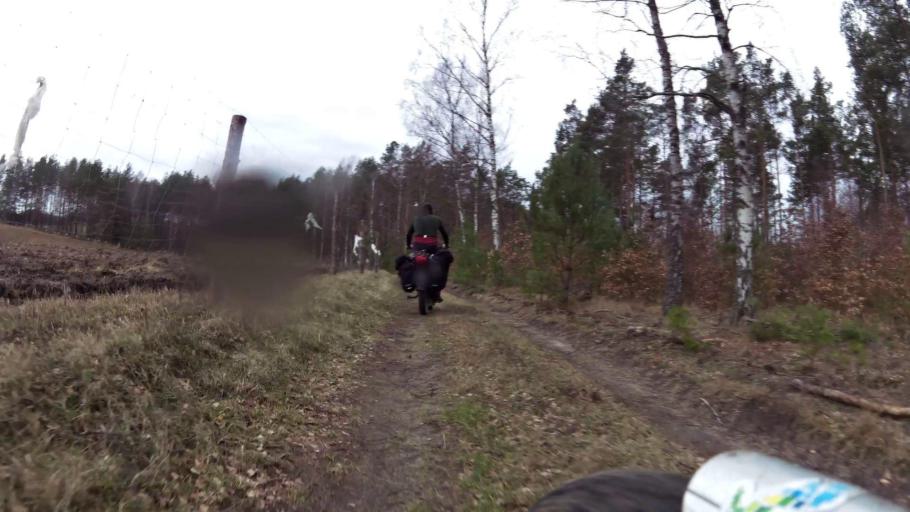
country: PL
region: Pomeranian Voivodeship
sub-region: Powiat bytowski
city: Trzebielino
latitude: 54.0846
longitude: 17.1207
